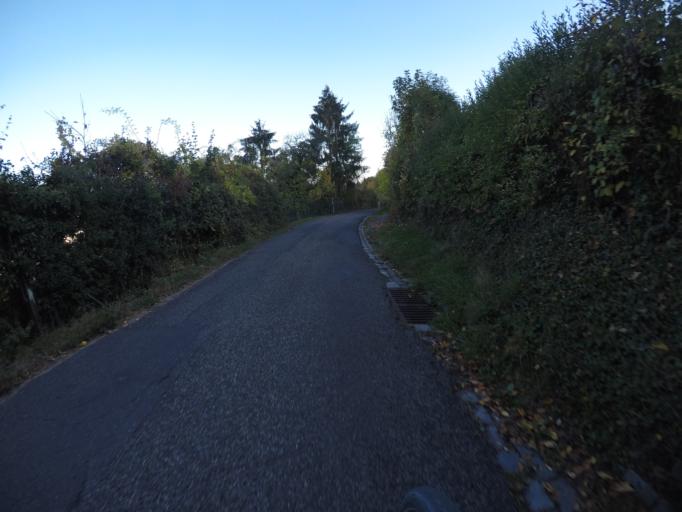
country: DE
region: Baden-Wuerttemberg
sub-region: Regierungsbezirk Stuttgart
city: Stuttgart-Ost
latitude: 48.7662
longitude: 9.2427
